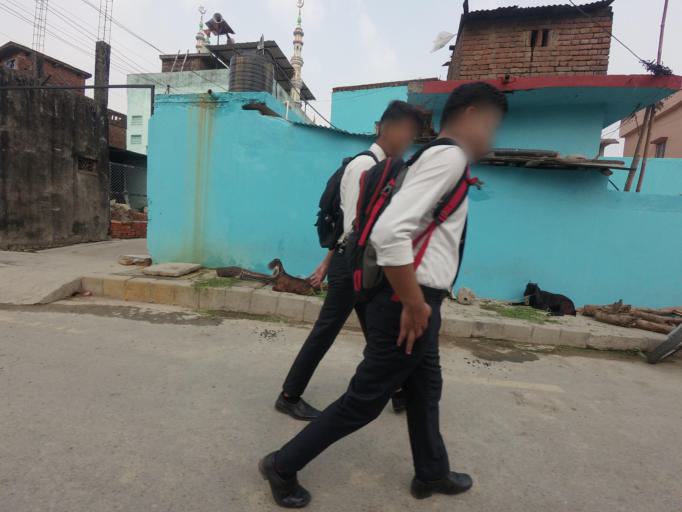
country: NP
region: Western Region
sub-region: Lumbini Zone
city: Bhairahawa
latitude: 27.4977
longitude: 83.4505
